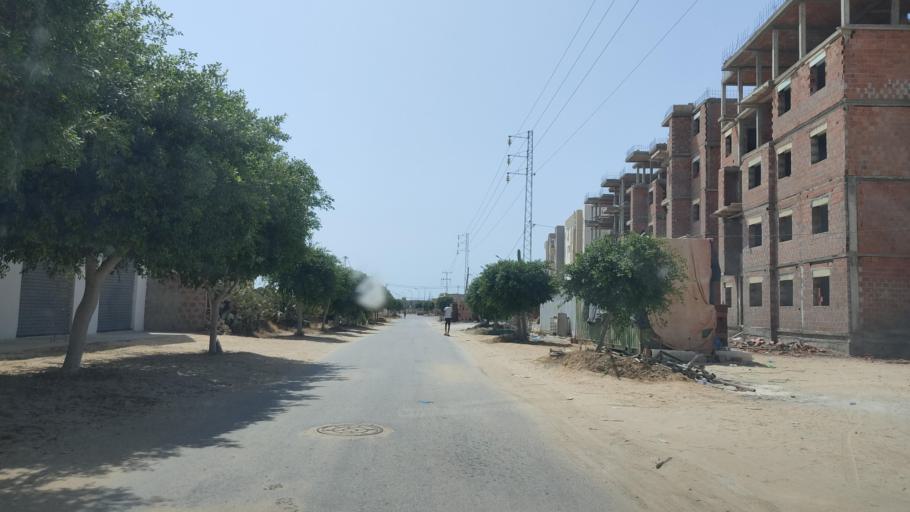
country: TN
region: Safaqis
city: Sfax
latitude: 34.6696
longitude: 10.7061
